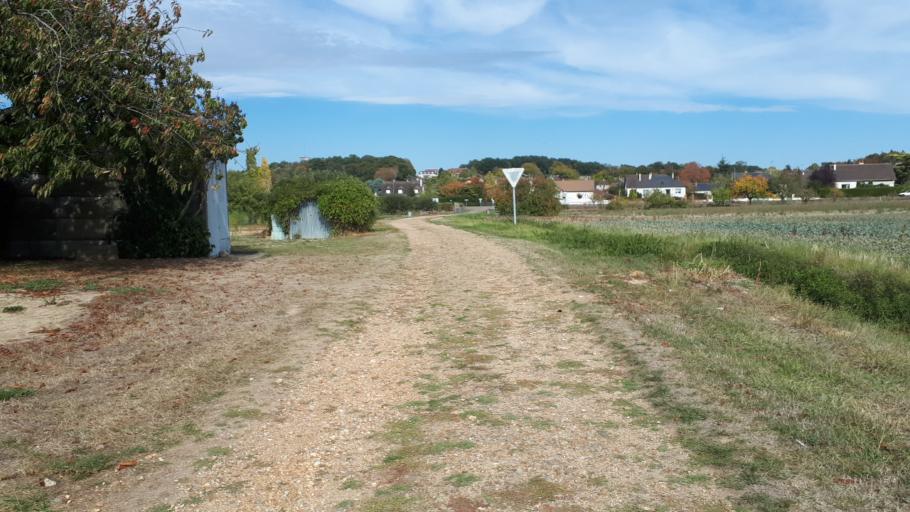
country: FR
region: Centre
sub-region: Departement du Loir-et-Cher
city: Villiers-sur-Loir
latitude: 47.8006
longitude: 0.9955
